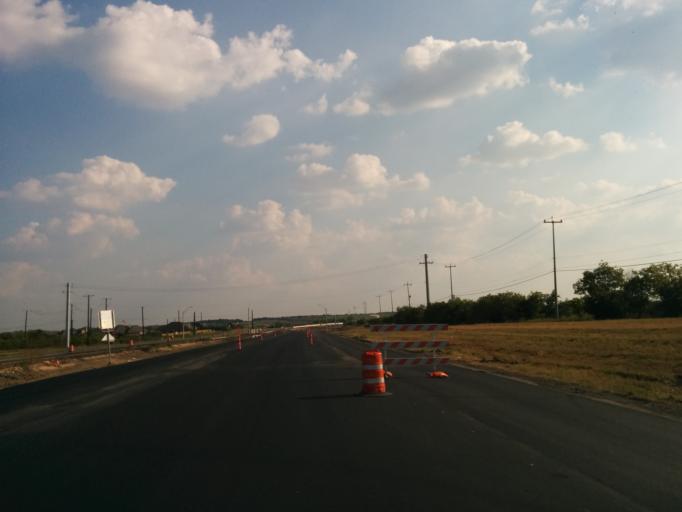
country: US
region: Texas
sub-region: Bexar County
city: Converse
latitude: 29.4932
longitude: -98.2902
